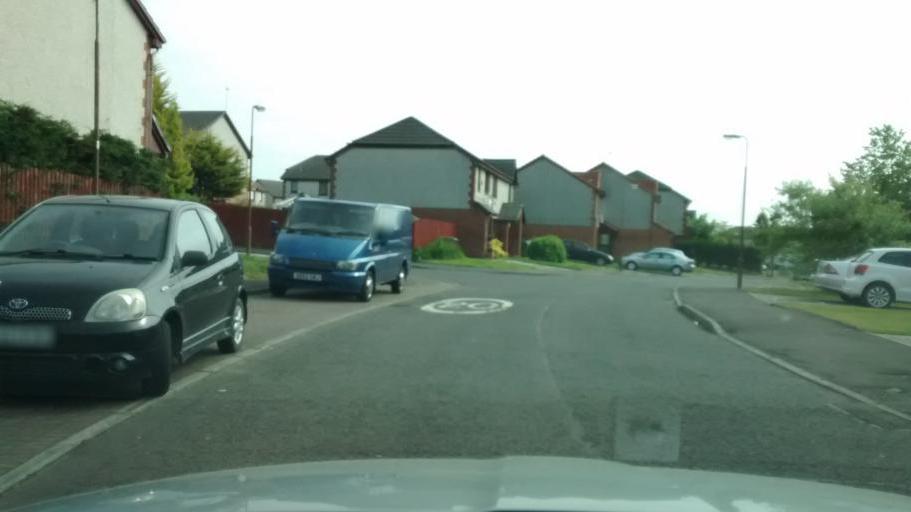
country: GB
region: Scotland
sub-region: West Lothian
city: Mid Calder
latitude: 55.8981
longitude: -3.4948
